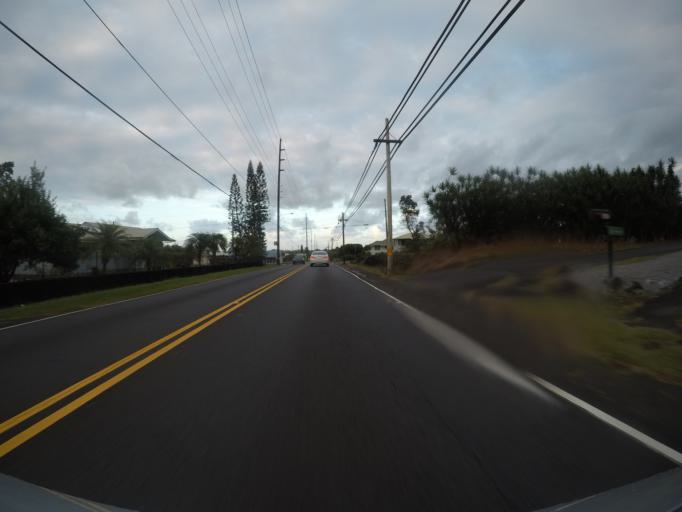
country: US
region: Hawaii
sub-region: Hawaii County
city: Hilo
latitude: 19.6842
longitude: -155.0753
